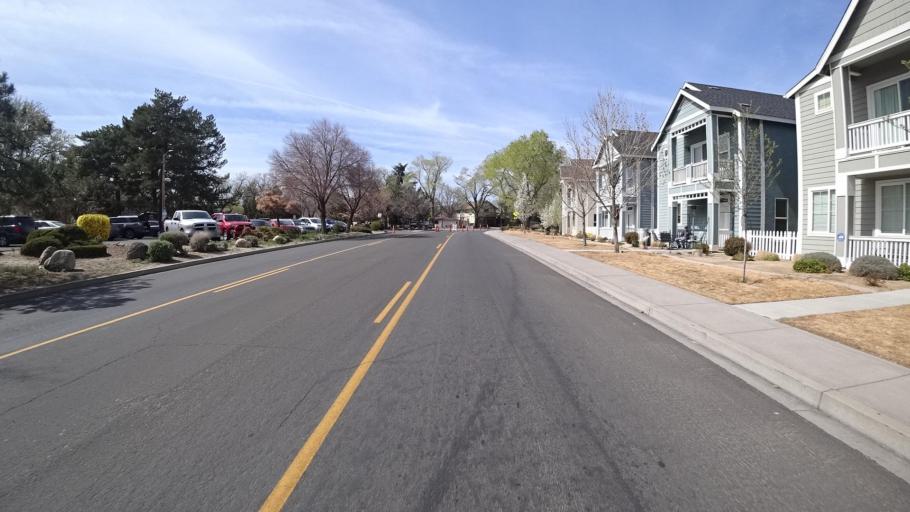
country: US
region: Nevada
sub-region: Washoe County
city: Reno
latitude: 39.5034
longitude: -119.8063
